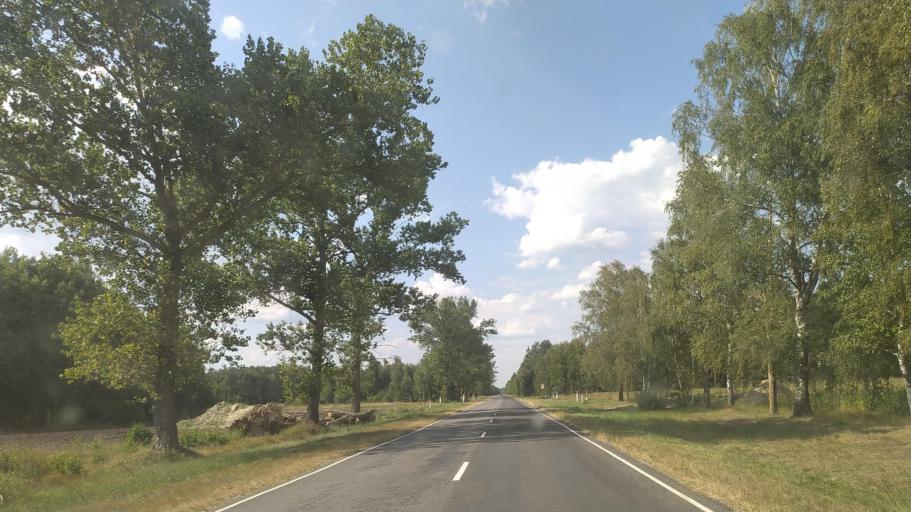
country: BY
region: Brest
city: Drahichyn
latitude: 52.2109
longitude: 25.1371
